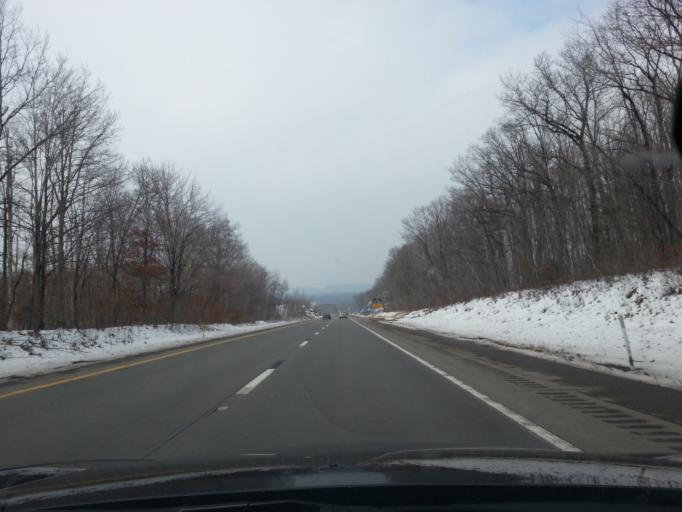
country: US
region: Pennsylvania
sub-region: Luzerne County
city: Freeland
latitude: 41.0918
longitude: -75.9621
